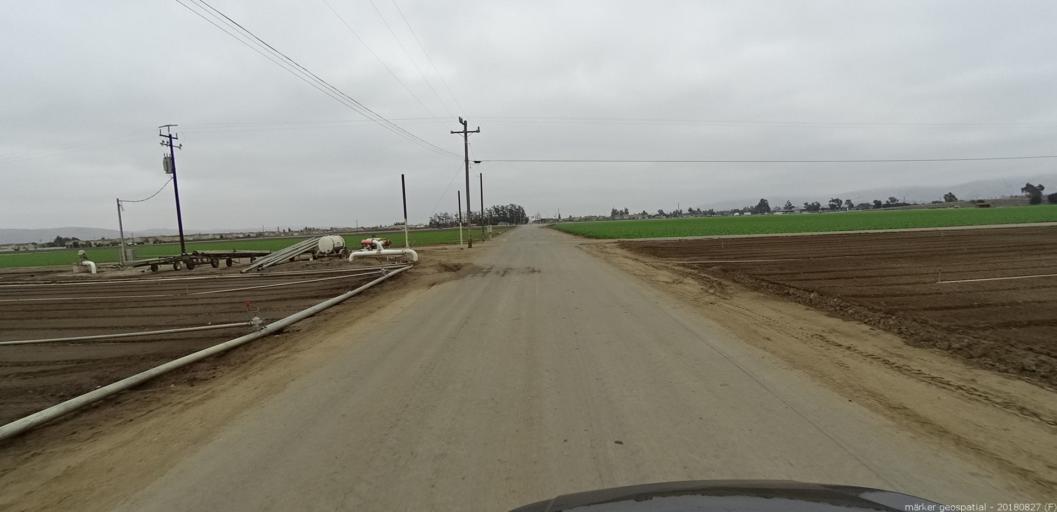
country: US
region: California
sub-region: Monterey County
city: Greenfield
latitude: 36.3354
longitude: -121.2422
